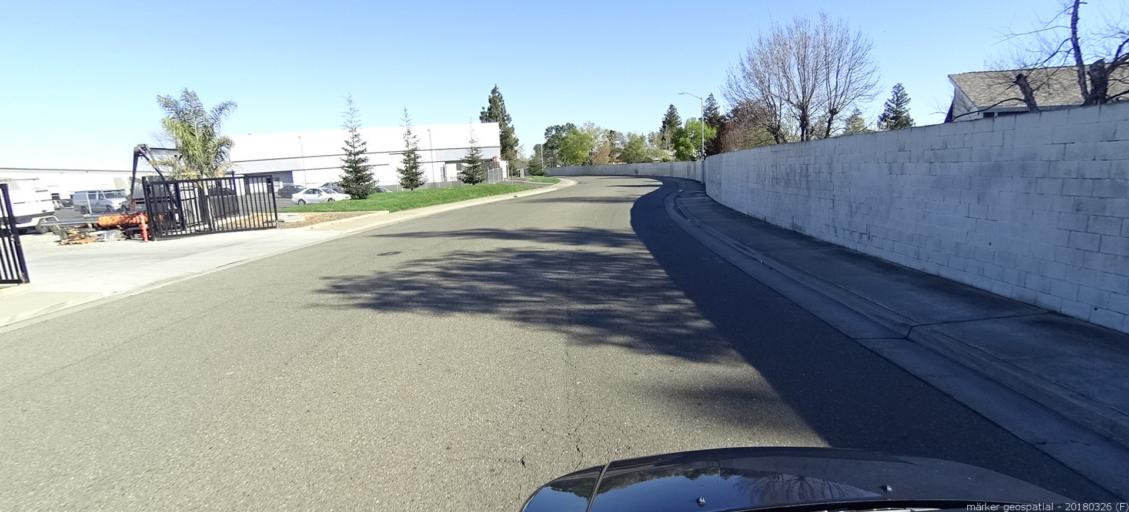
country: US
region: California
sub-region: Sacramento County
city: Florin
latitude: 38.4784
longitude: -121.3884
